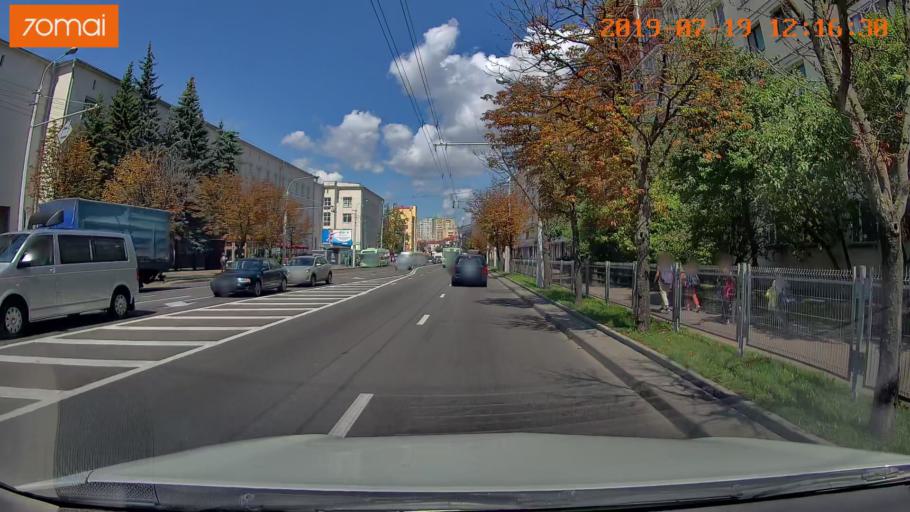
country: BY
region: Minsk
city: Minsk
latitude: 53.9207
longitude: 27.6022
